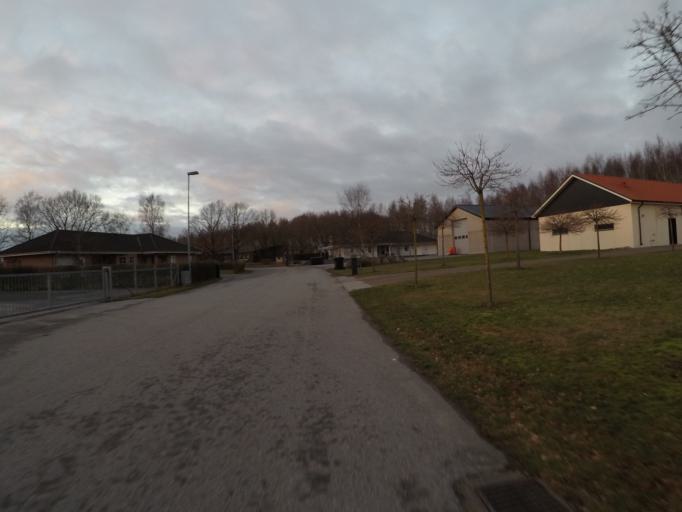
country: SE
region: Skane
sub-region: Sjobo Kommun
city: Sjoebo
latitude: 55.6451
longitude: 13.6954
